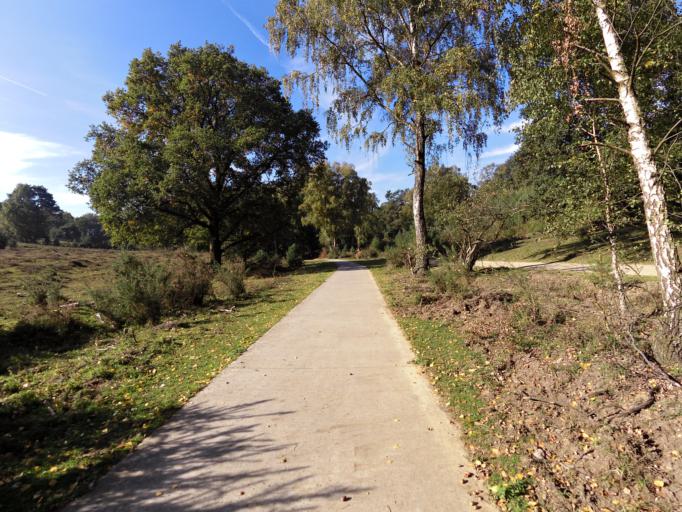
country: NL
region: Gelderland
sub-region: Gemeente Rheden
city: Velp
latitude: 52.0125
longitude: 5.9974
